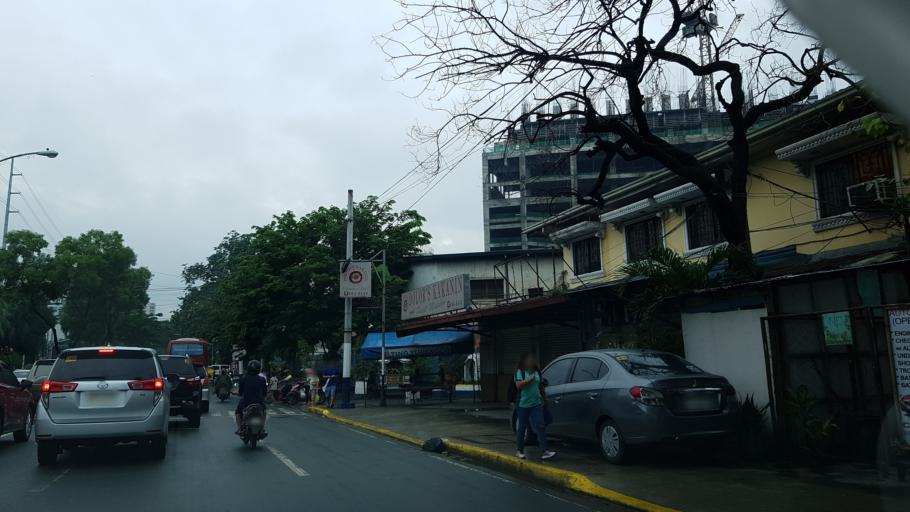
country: PH
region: Metro Manila
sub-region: City of Manila
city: Quiapo
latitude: 14.5753
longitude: 120.9955
